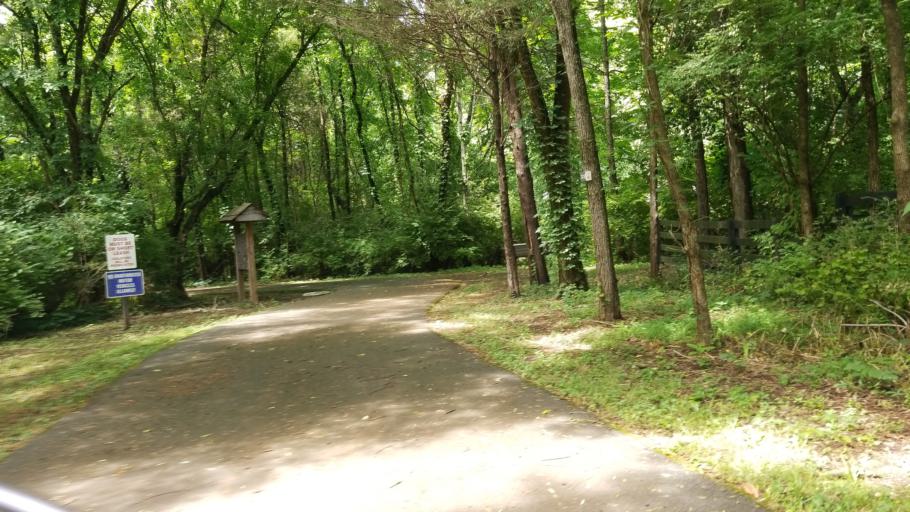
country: US
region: Tennessee
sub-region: Davidson County
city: Forest Hills
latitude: 36.0339
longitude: -86.8359
